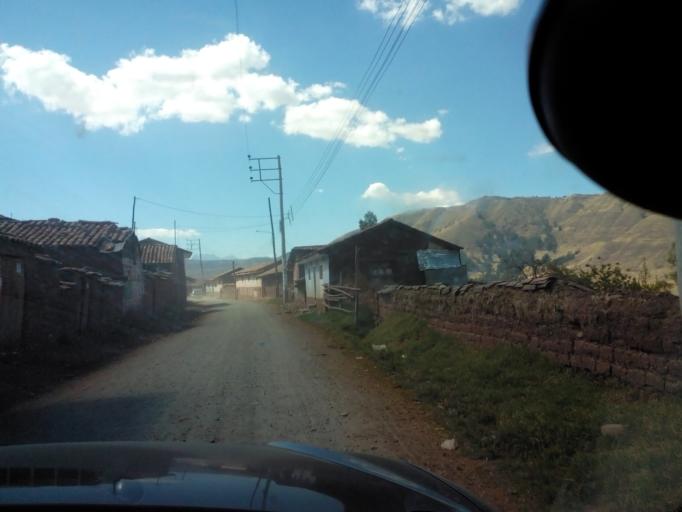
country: PE
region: Cusco
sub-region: Provincia de Anta
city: Huarocondo
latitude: -13.4360
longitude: -72.2259
